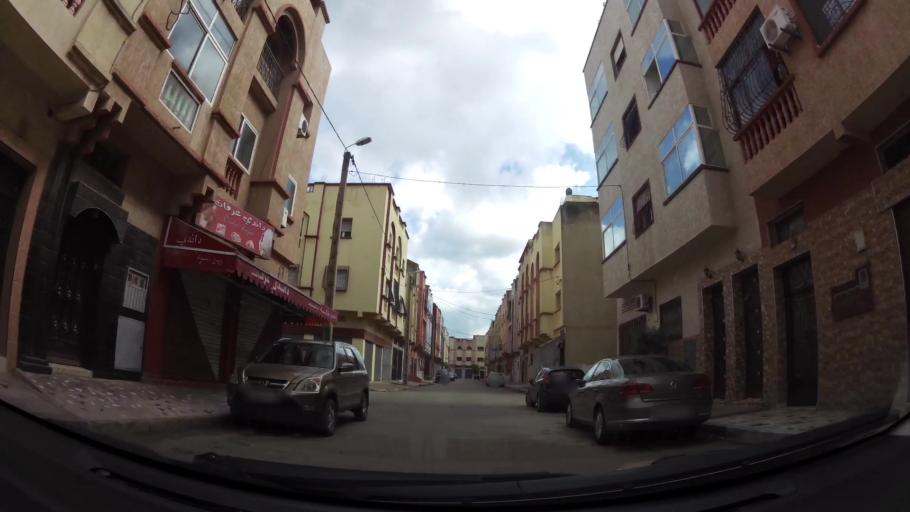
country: MA
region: Chaouia-Ouardigha
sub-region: Settat Province
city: Berrechid
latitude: 33.2745
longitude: -7.5886
